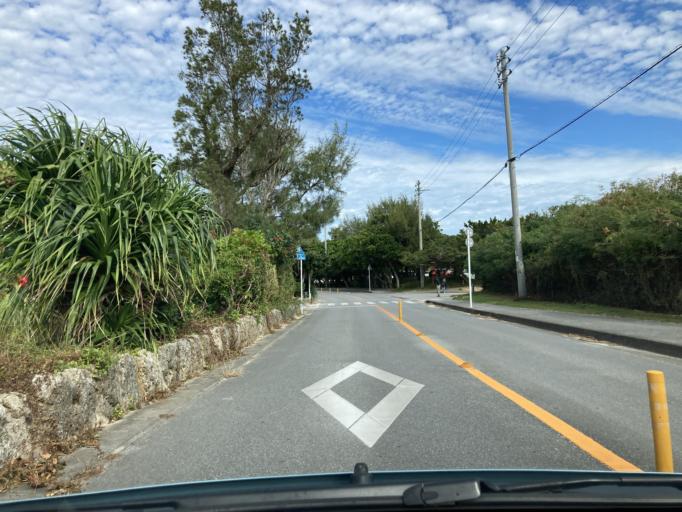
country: JP
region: Okinawa
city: Ishikawa
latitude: 26.4355
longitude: 127.7164
